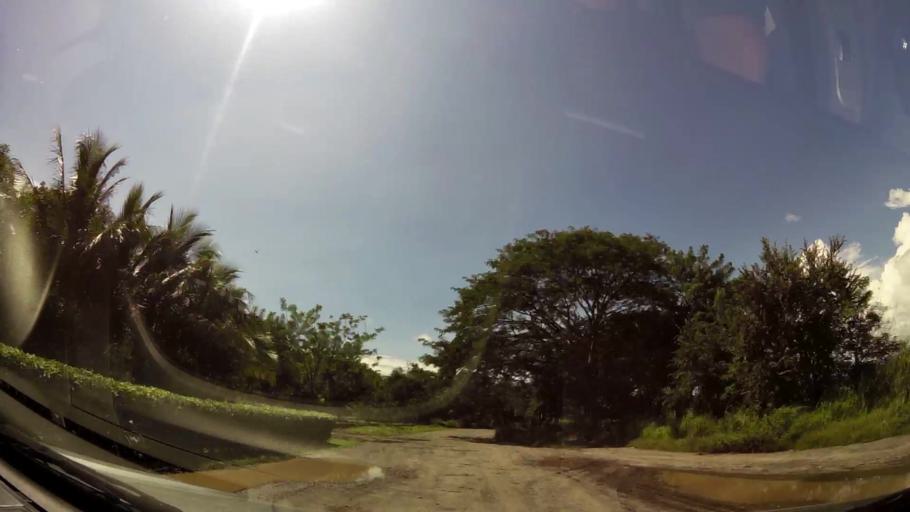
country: PA
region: Panama
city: Nueva Gorgona
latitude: 8.5575
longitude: -79.8566
